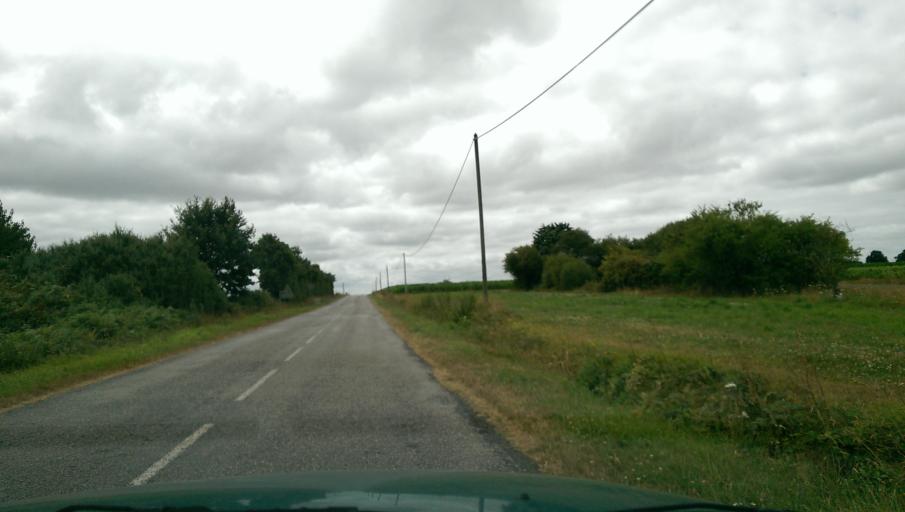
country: FR
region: Pays de la Loire
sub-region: Departement de la Loire-Atlantique
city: Remouille
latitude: 47.0419
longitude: -1.3951
